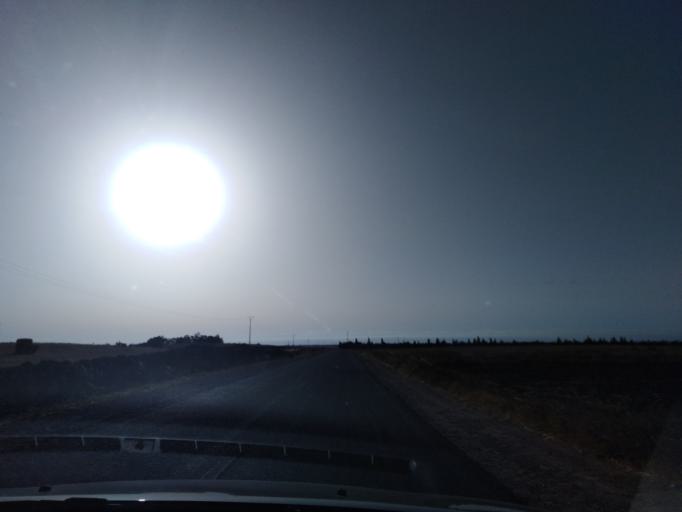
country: MA
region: Doukkala-Abda
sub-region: Safi
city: Safi
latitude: 32.4800
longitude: -8.9057
